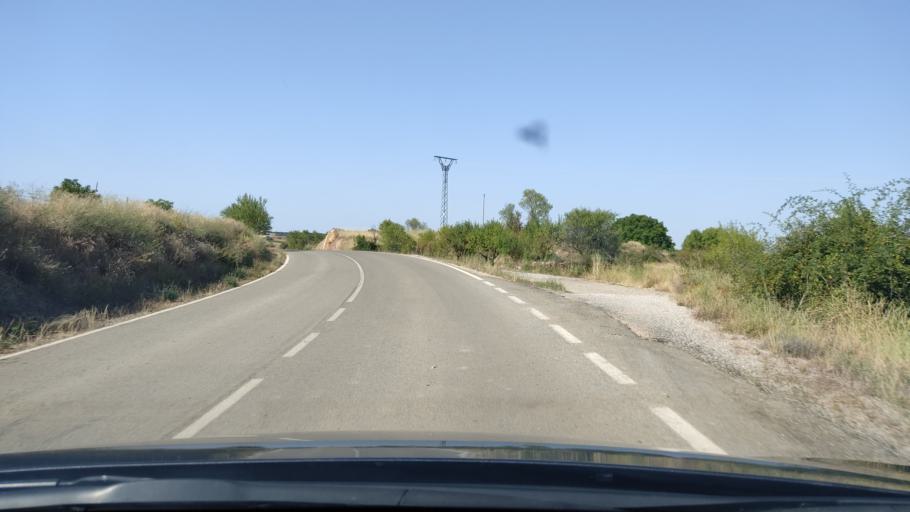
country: ES
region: Aragon
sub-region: Provincia de Teruel
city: Cucalon
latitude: 41.0840
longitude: -1.2192
